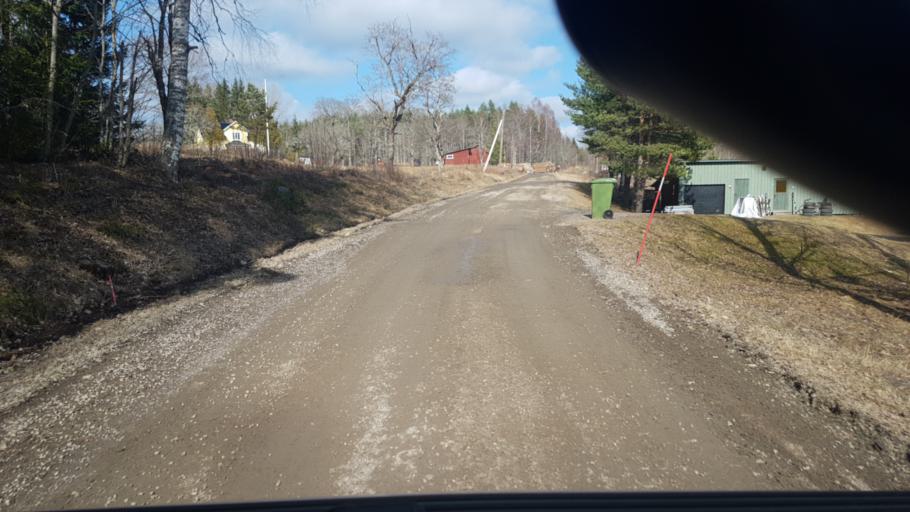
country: SE
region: Vaermland
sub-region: Eda Kommun
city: Amotfors
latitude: 59.8089
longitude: 12.4415
